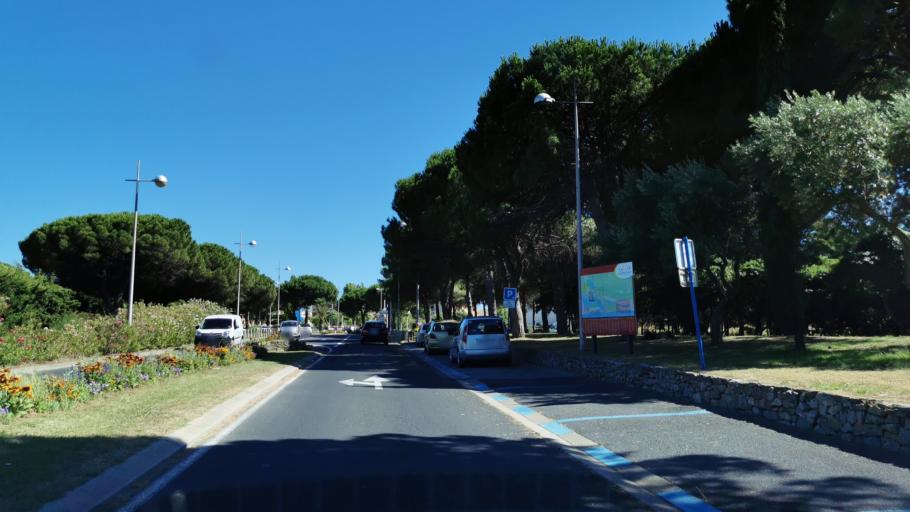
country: FR
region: Languedoc-Roussillon
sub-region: Departement de l'Aude
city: Gruissan
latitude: 43.1135
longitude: 3.0930
